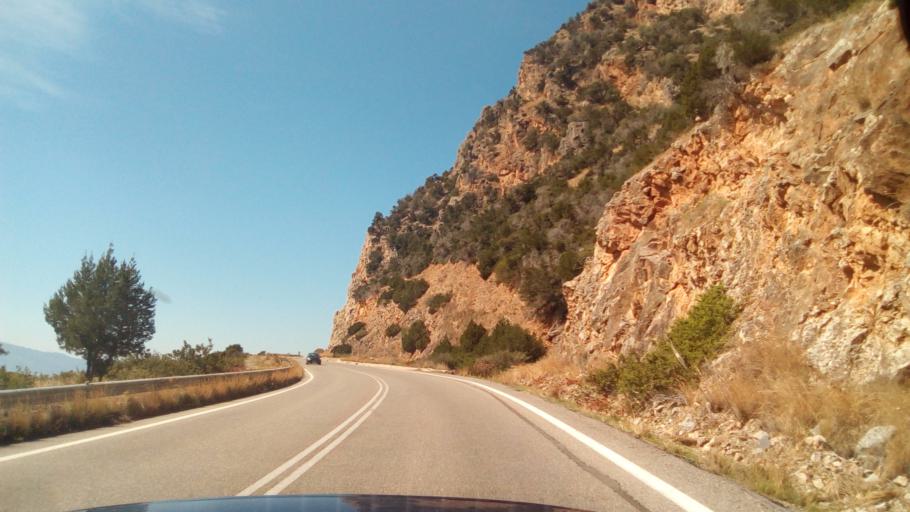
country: GR
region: West Greece
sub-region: Nomos Achaias
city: Aigio
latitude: 38.3594
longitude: 22.1367
